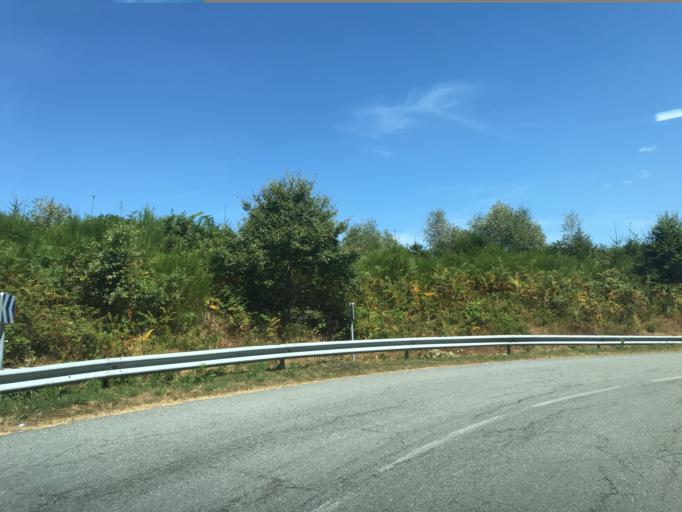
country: FR
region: Limousin
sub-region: Departement de la Creuse
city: Felletin
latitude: 45.7830
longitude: 2.1416
